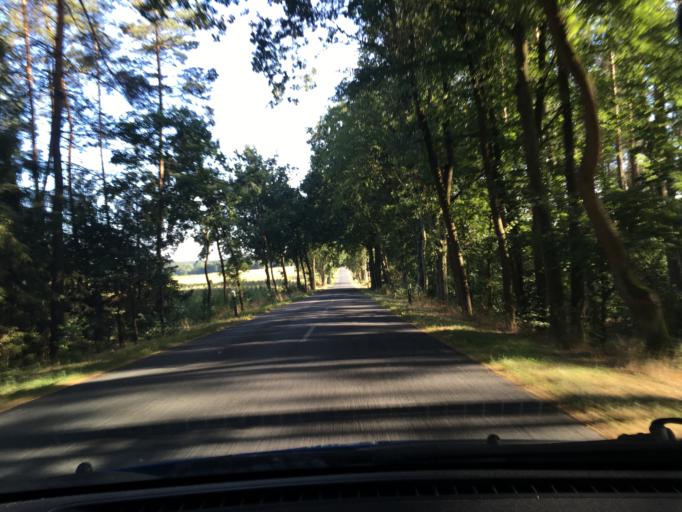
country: DE
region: Lower Saxony
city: Thomasburg
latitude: 53.2339
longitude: 10.7038
